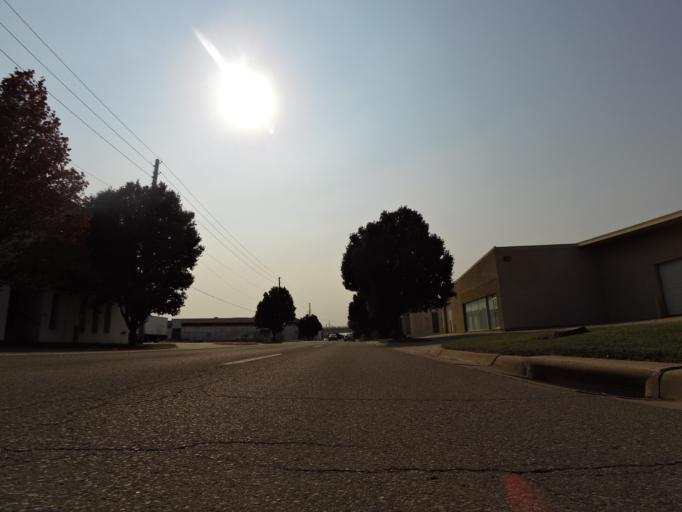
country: US
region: Kansas
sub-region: Sedgwick County
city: Wichita
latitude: 37.6976
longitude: -97.3276
